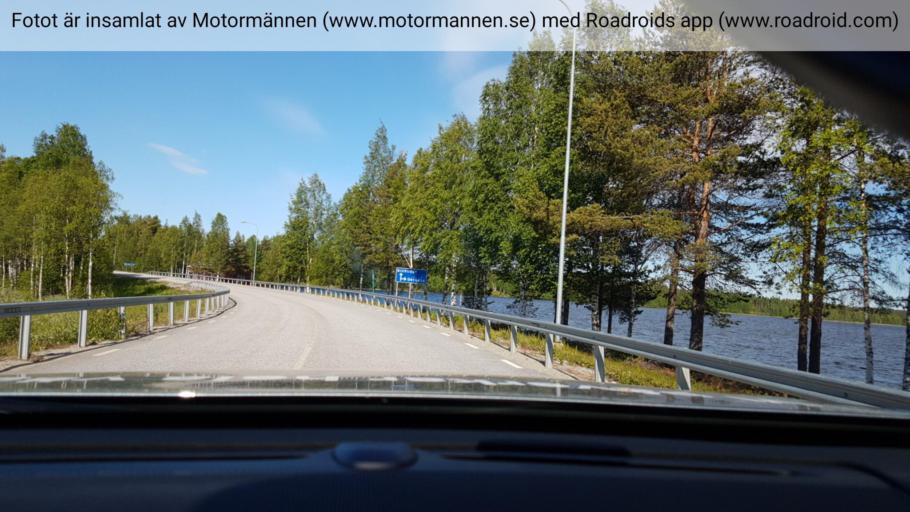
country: SE
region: Vaesterbotten
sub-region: Bjurholms Kommun
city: Bjurholm
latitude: 64.1462
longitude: 19.3218
